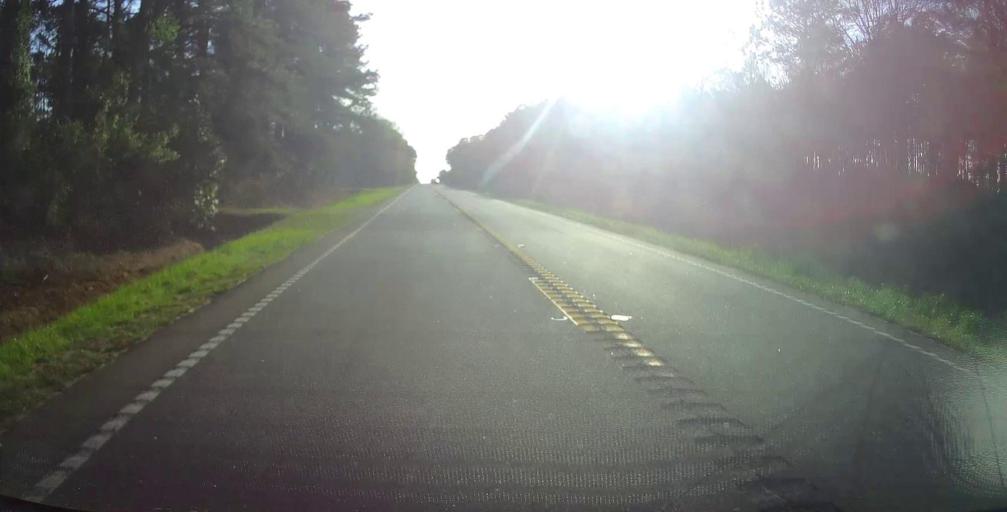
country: US
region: Georgia
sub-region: Tattnall County
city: Reidsville
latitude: 32.1245
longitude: -82.0610
